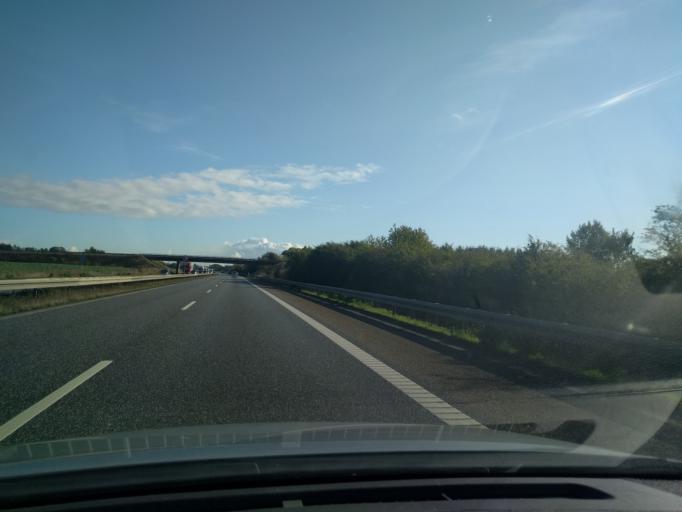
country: DK
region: Zealand
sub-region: Soro Kommune
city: Frederiksberg
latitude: 55.4486
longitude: 11.6533
